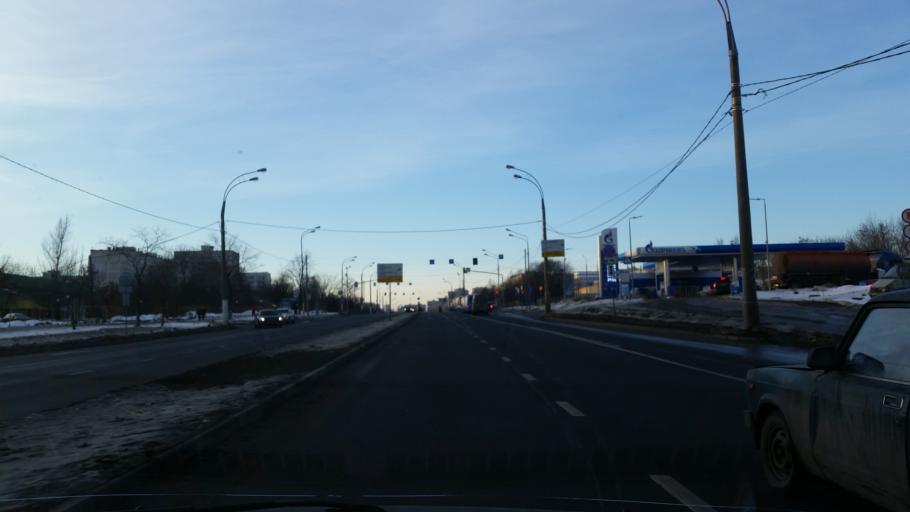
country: RU
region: Moscow
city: Chertanovo Yuzhnoye
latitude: 55.6085
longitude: 37.6188
